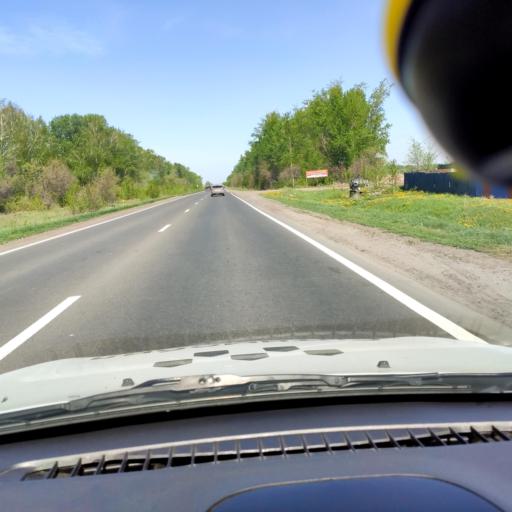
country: RU
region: Samara
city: Tol'yatti
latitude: 53.6238
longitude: 49.3076
